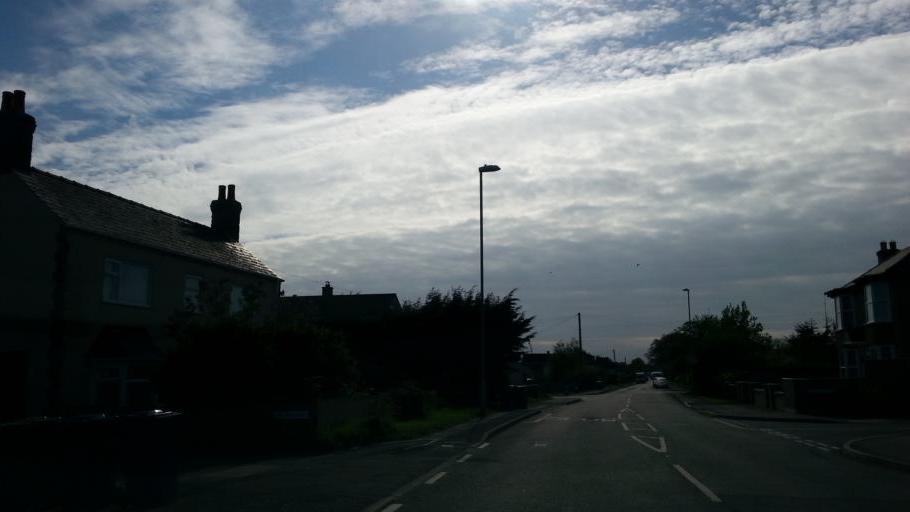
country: GB
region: England
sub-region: Cambridgeshire
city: Chatteris
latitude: 52.4576
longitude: 0.0639
